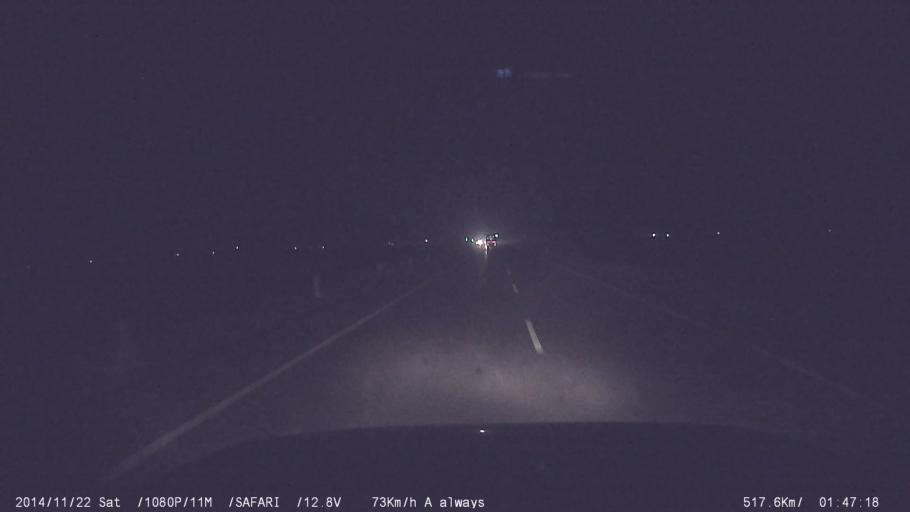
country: IN
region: Tamil Nadu
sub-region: Villupuram
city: Chinna Salem
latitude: 11.6457
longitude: 78.8805
